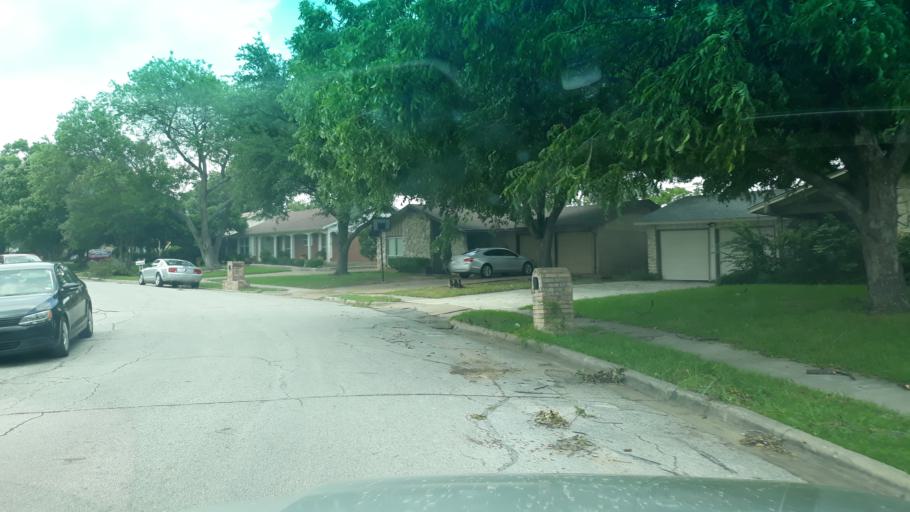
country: US
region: Texas
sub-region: Dallas County
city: Irving
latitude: 32.8518
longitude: -96.9949
